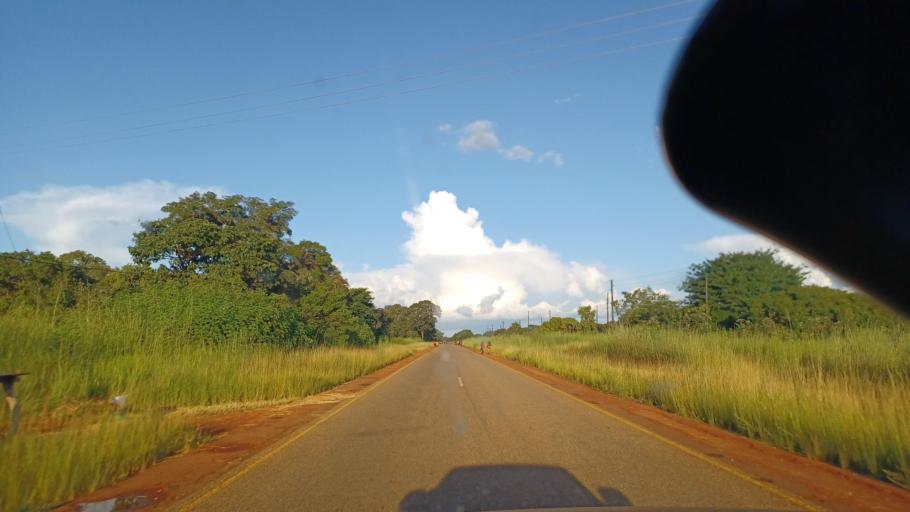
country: ZM
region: North-Western
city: Kalengwa
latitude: -13.1437
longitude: 25.0439
